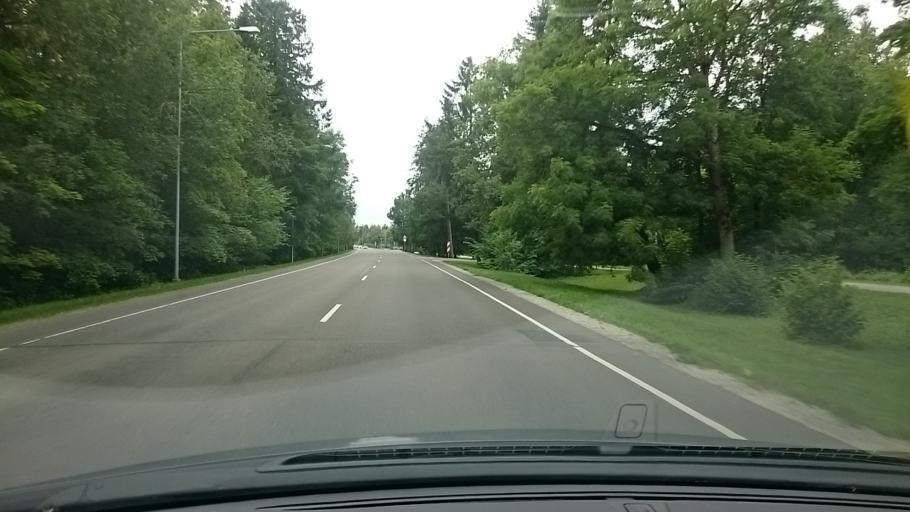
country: EE
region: Harju
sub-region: Harku vald
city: Tabasalu
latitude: 59.4344
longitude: 24.5225
